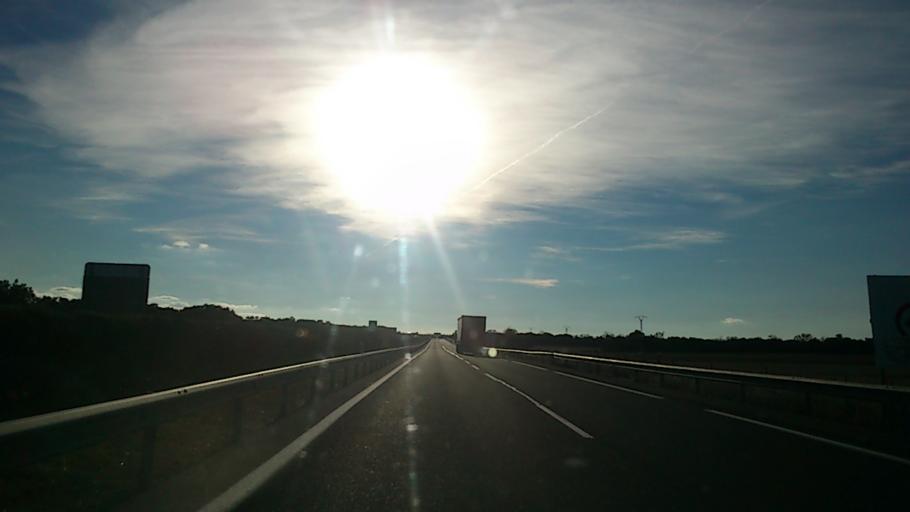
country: ES
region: Castille-La Mancha
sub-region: Provincia de Guadalajara
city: Mirabueno
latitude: 40.9244
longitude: -2.7220
